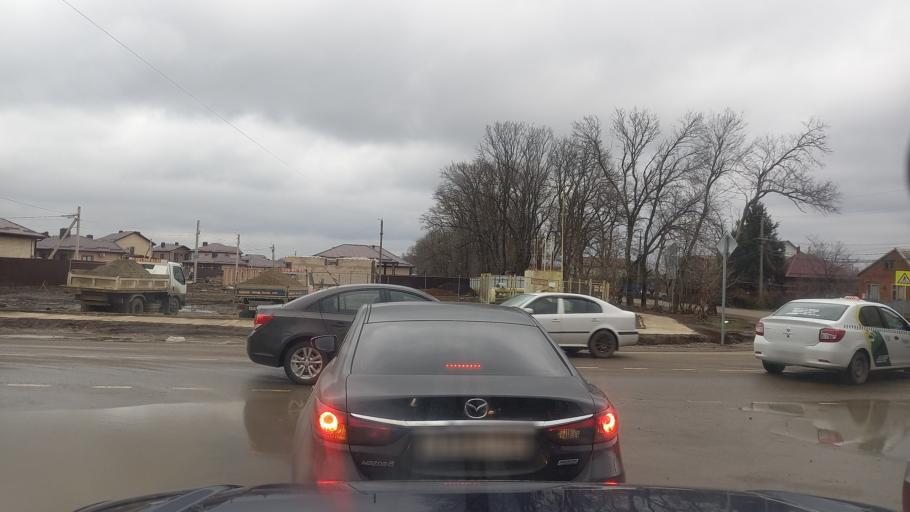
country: RU
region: Krasnodarskiy
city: Pashkovskiy
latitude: 45.0593
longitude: 39.1739
